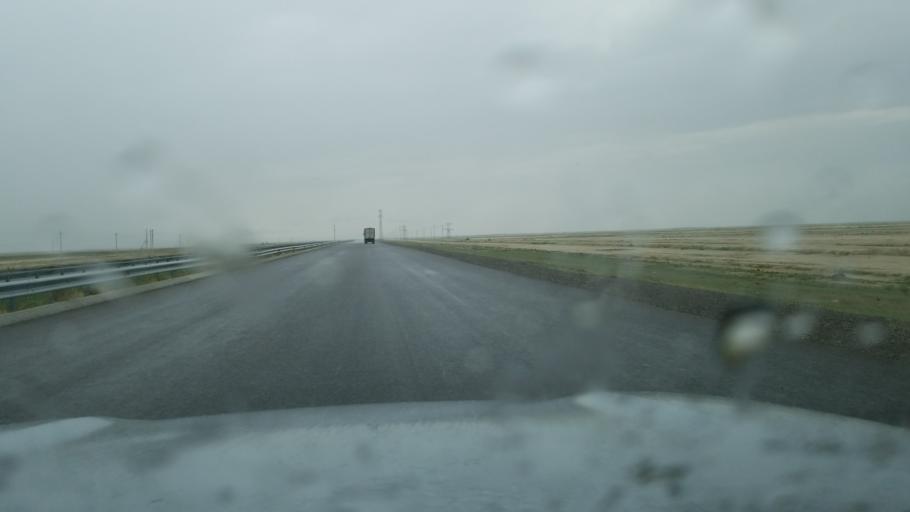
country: TM
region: Balkan
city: Serdar
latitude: 39.0186
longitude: 56.2149
